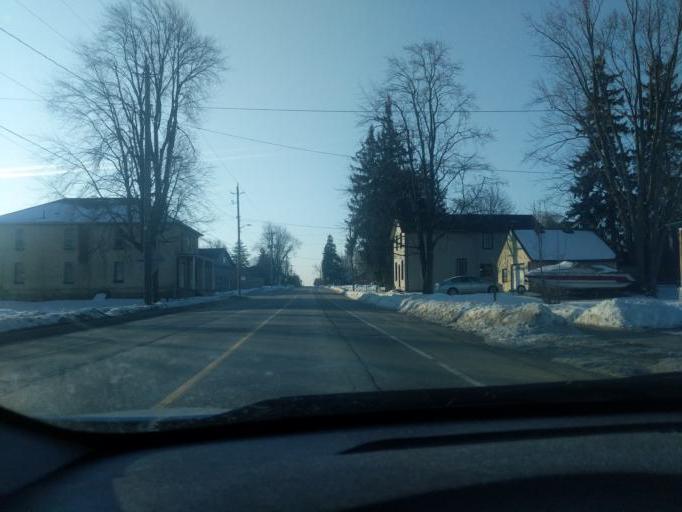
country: CA
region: Ontario
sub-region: Oxford County
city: Woodstock
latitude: 43.2700
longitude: -80.6573
